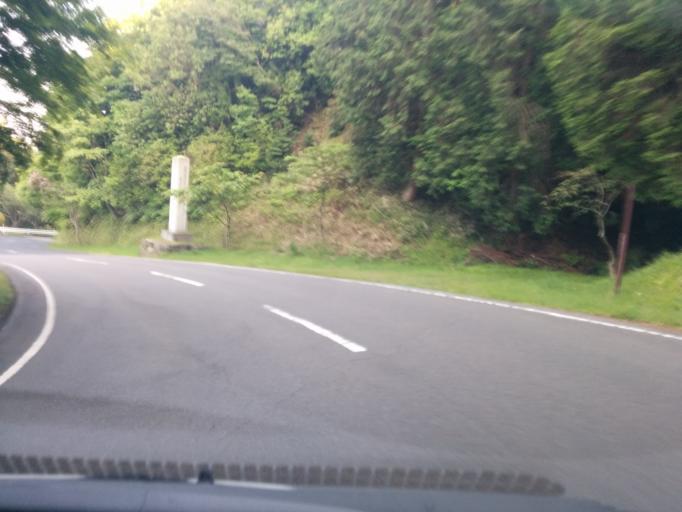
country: JP
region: Shiga Prefecture
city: Kitahama
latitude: 35.1035
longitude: 135.8602
